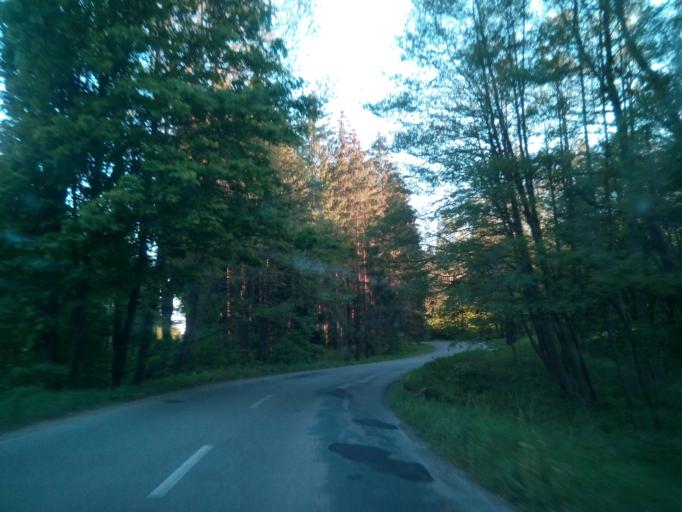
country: CZ
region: South Moravian
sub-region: Okres Blansko
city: Jedovnice
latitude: 49.3120
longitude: 16.7467
